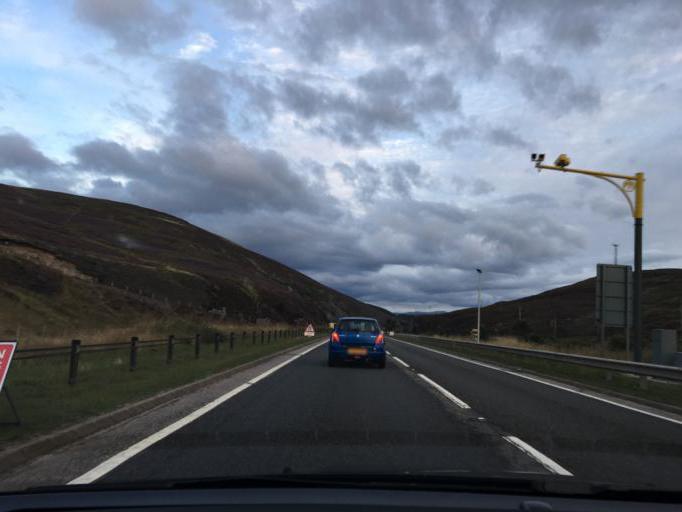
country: GB
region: Scotland
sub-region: Highland
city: Aviemore
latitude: 57.3072
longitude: -3.9367
